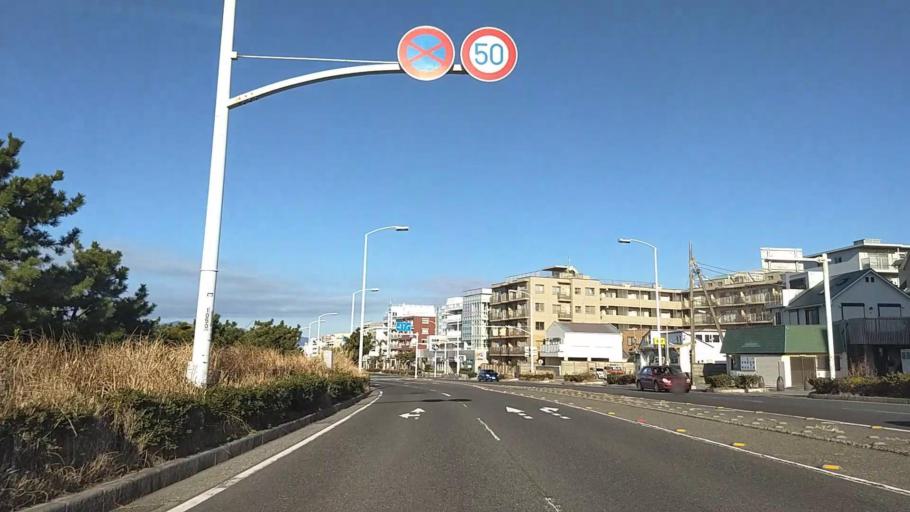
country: JP
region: Kanagawa
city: Fujisawa
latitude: 35.3130
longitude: 139.4770
